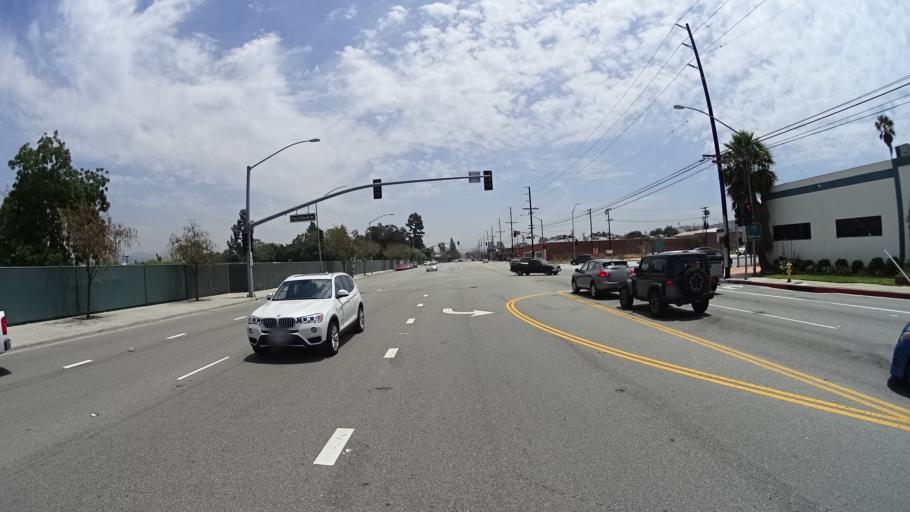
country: US
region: California
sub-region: Los Angeles County
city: Burbank
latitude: 34.1652
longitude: -118.2944
